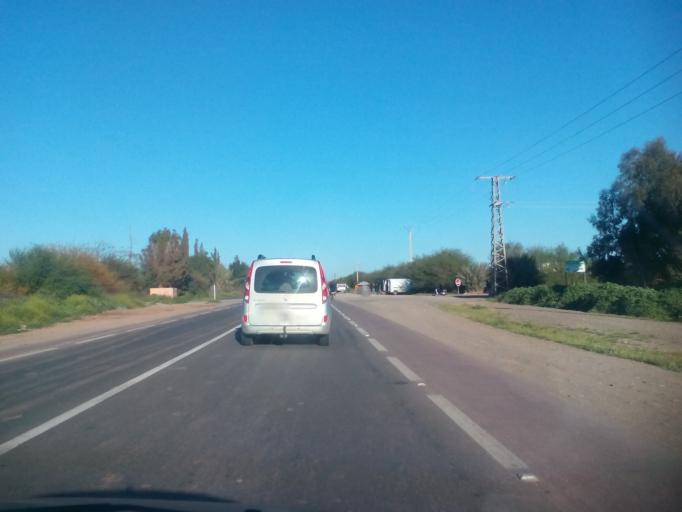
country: MA
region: Marrakech-Tensift-Al Haouz
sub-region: Marrakech
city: Marrakesh
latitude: 31.6297
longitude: -8.1446
